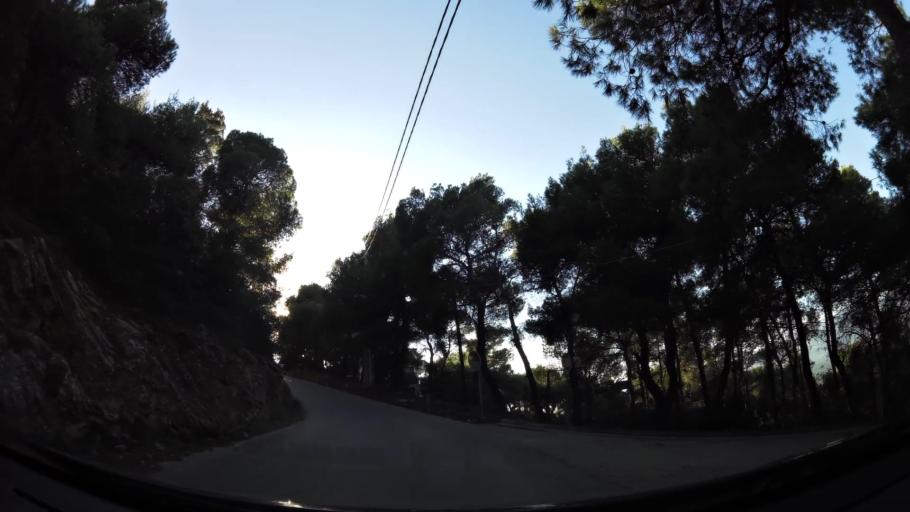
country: GR
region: Attica
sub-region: Nomarchia Athinas
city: Ekali
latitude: 38.0999
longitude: 23.8343
